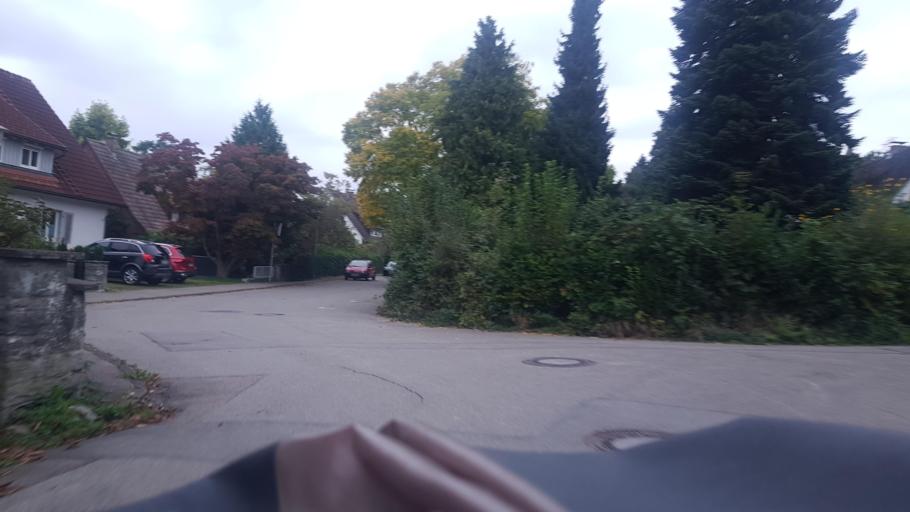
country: DE
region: Bavaria
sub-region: Swabia
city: Lindau
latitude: 47.5542
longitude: 9.6868
